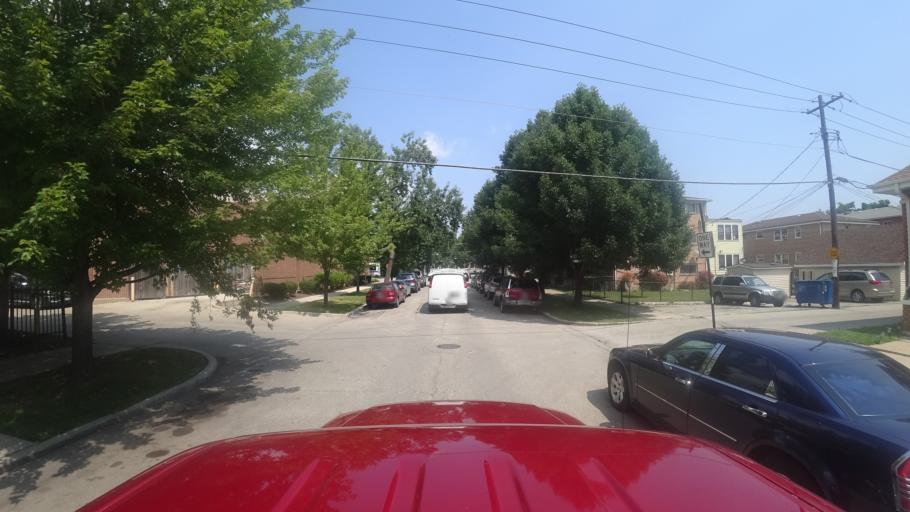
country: US
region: Illinois
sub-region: Cook County
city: Cicero
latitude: 41.8073
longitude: -87.7224
